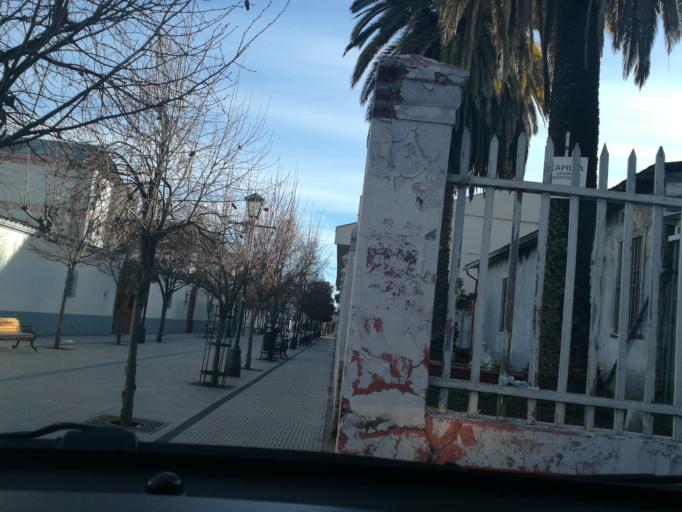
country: CL
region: O'Higgins
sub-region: Provincia de Cachapoal
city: Rancagua
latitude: -34.1746
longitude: -70.7416
